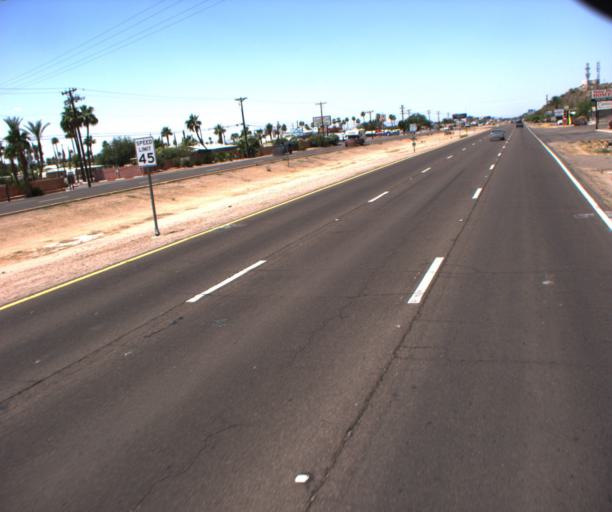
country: US
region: Arizona
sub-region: Pinal County
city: Apache Junction
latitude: 33.4154
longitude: -111.6440
